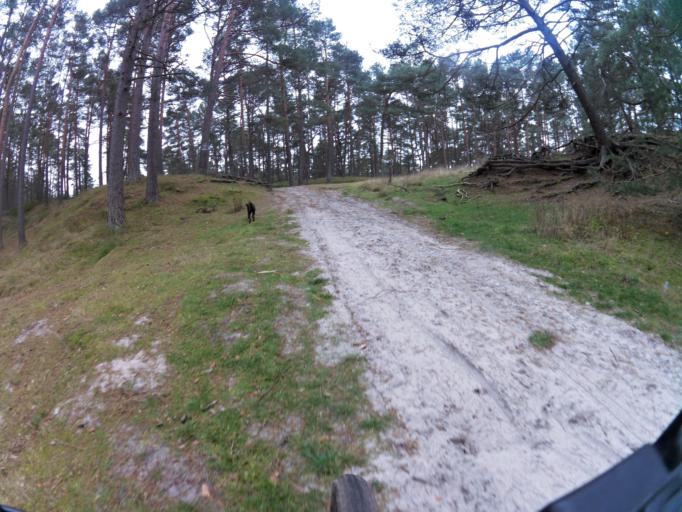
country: PL
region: West Pomeranian Voivodeship
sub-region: Powiat gryficki
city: Cerkwica
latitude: 54.1001
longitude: 15.1315
